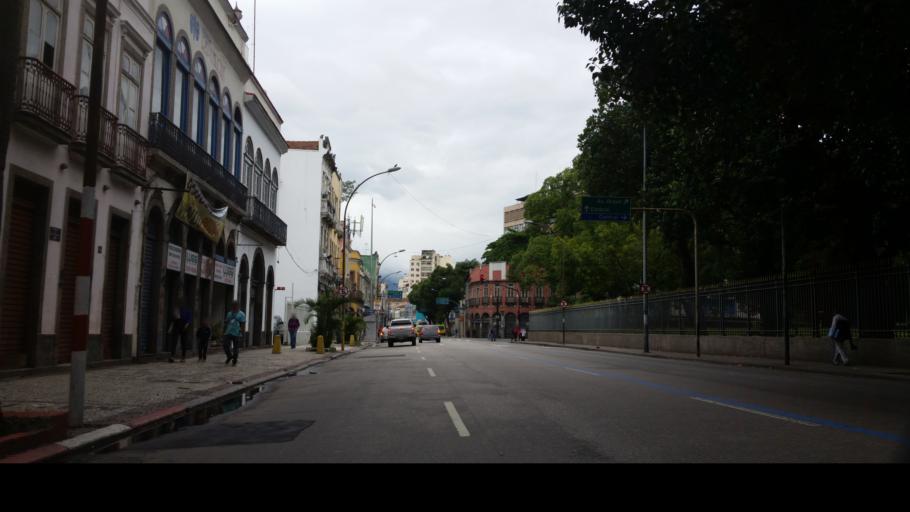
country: BR
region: Rio de Janeiro
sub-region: Rio De Janeiro
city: Rio de Janeiro
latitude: -22.9088
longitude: -43.1878
